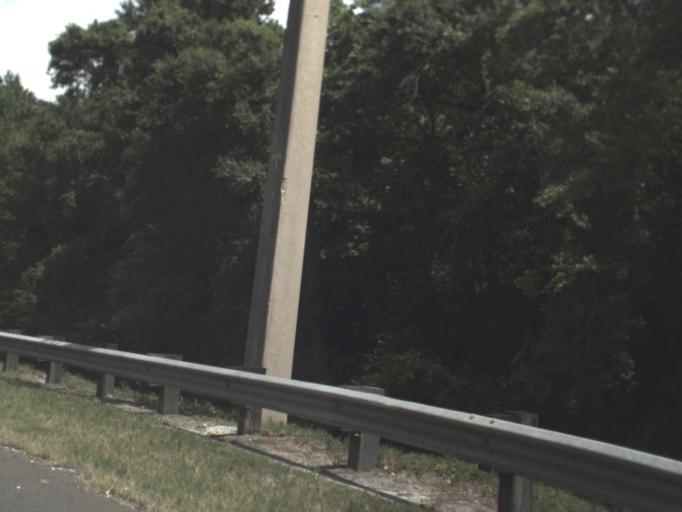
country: US
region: Florida
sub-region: Duval County
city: Jacksonville
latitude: 30.3570
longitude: -81.7101
